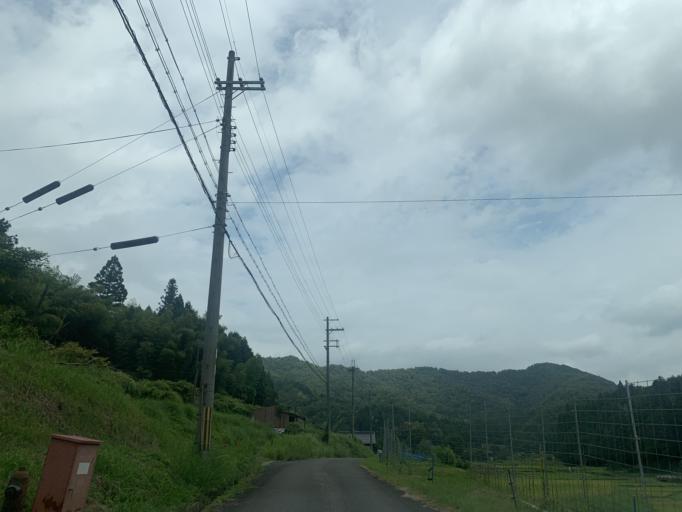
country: JP
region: Kyoto
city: Miyazu
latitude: 35.4437
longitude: 135.1589
